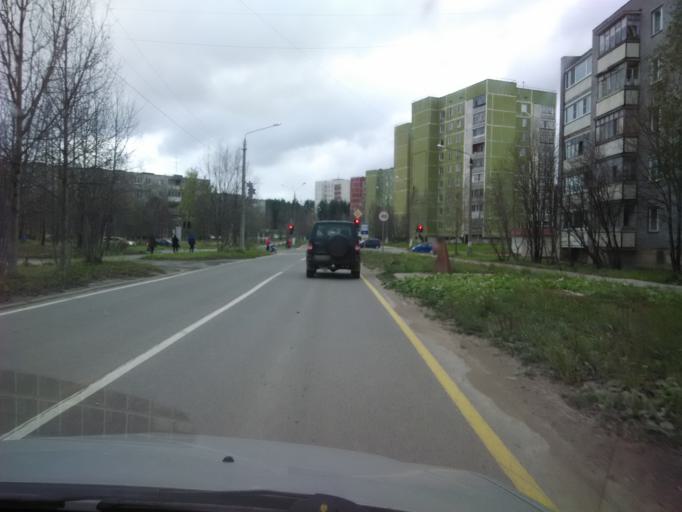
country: RU
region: Murmansk
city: Polyarnyye Zori
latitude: 67.3695
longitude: 32.4878
